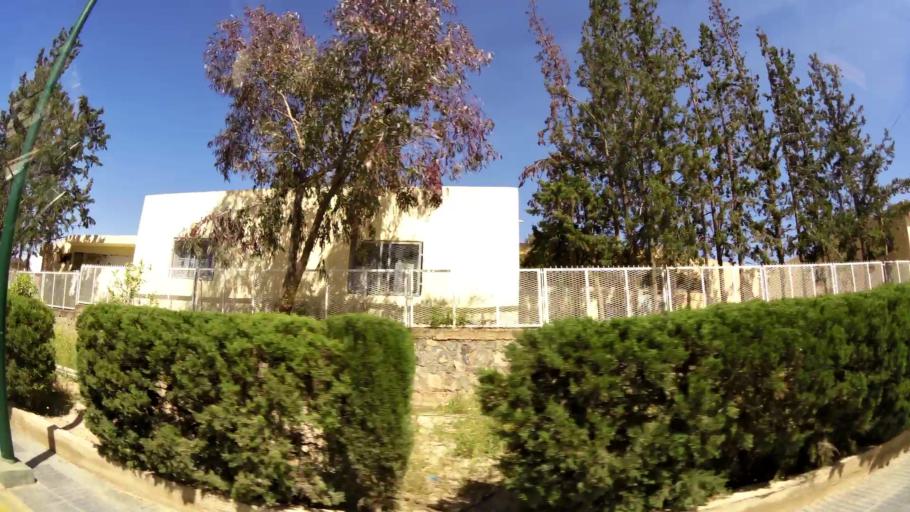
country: MA
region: Oriental
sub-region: Oujda-Angad
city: Oujda
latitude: 34.6510
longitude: -1.9063
